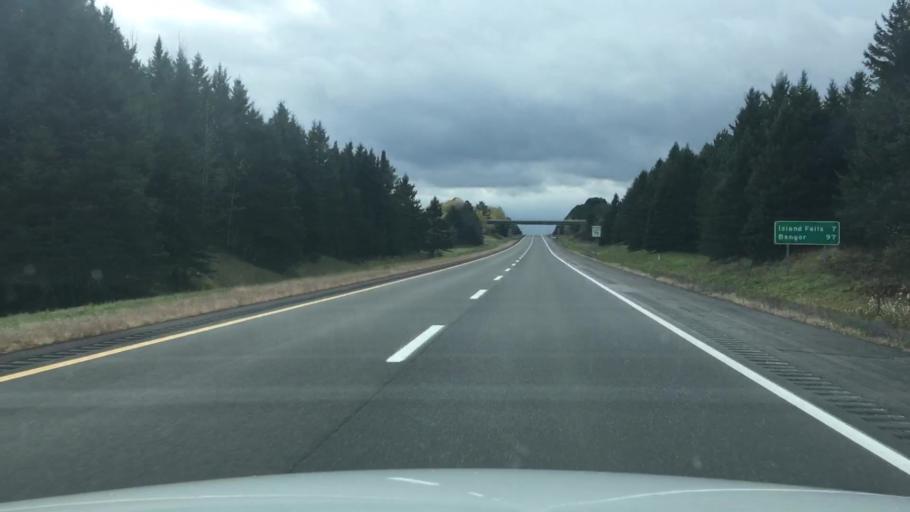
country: US
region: Maine
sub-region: Penobscot County
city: Patten
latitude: 46.1009
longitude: -68.1817
